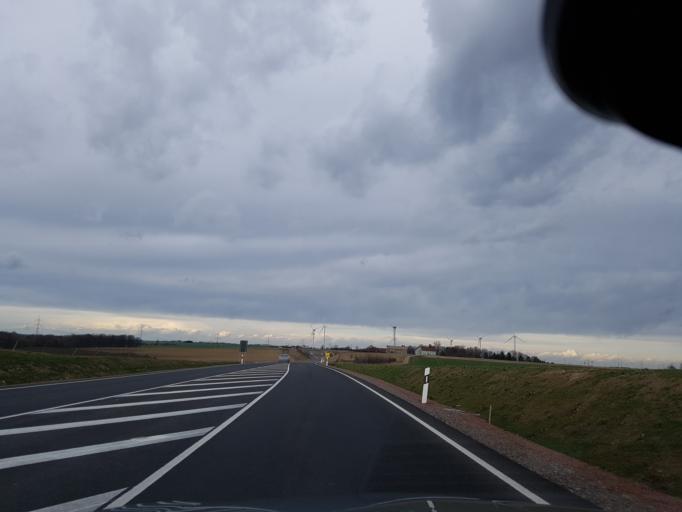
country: DE
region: Saxony
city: Niederstriegis
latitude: 51.0473
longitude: 13.1172
